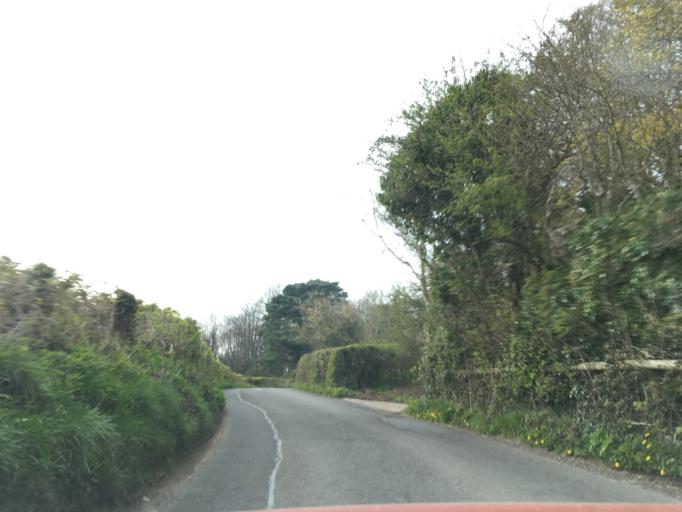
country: GB
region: Wales
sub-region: Cardiff
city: Radyr
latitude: 51.5402
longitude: -3.2348
